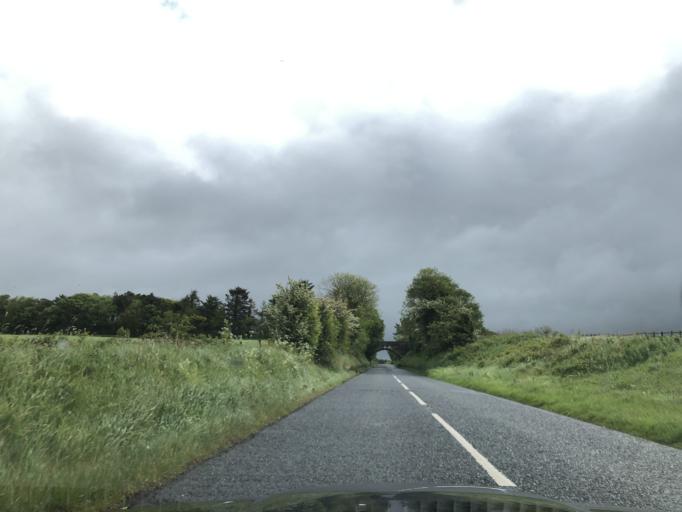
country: GB
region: Northern Ireland
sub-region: Moyle District
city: Ballycastle
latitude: 55.1610
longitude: -6.3788
